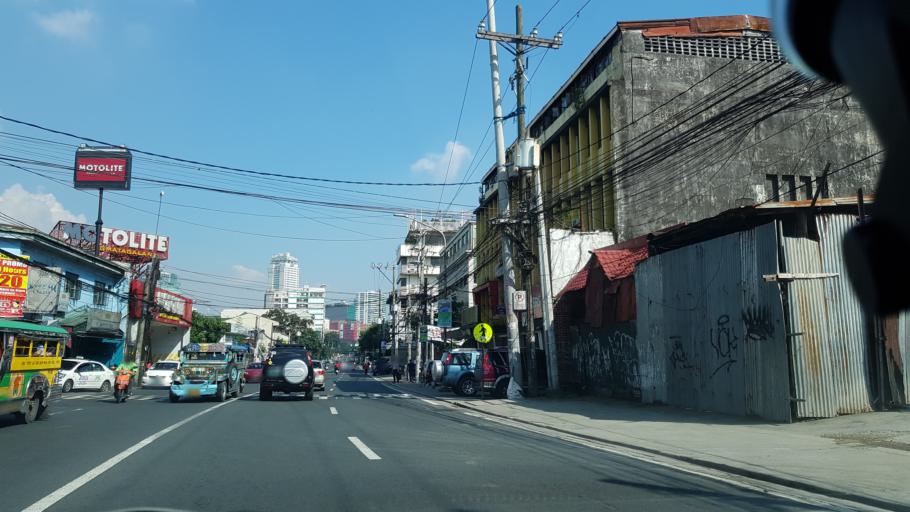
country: PH
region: Metro Manila
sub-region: Quezon City
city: Quezon City
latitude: 14.6245
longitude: 121.0423
